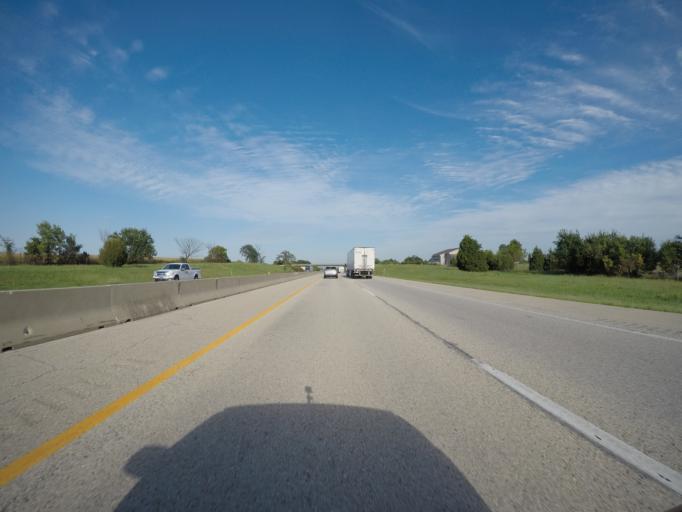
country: US
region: Kansas
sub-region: Douglas County
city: Lawrence
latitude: 38.9979
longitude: -95.3190
